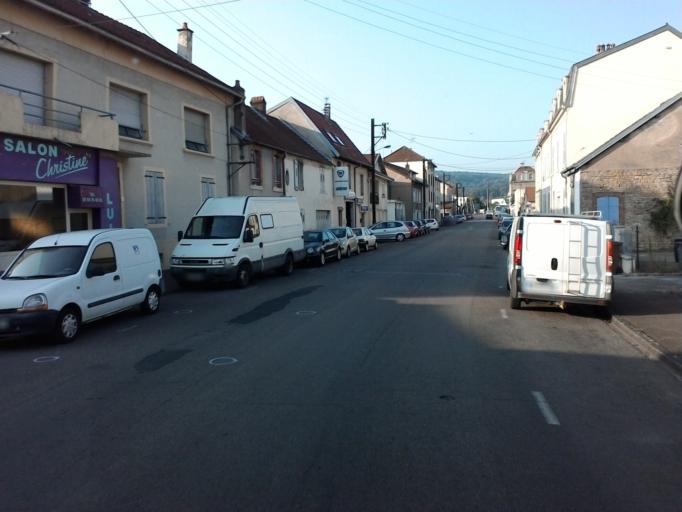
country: FR
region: Franche-Comte
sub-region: Departement de la Haute-Saone
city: Navenne
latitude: 47.6192
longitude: 6.1612
